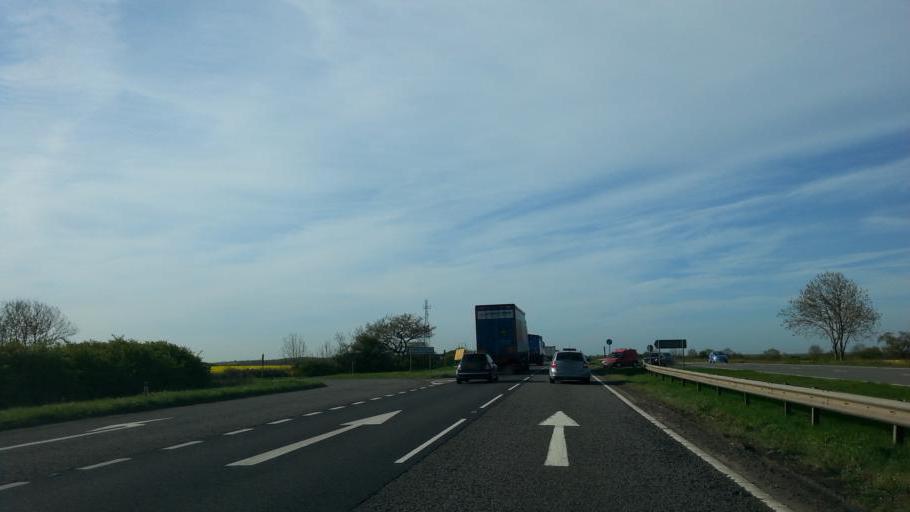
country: GB
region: England
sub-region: District of Rutland
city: Clipsham
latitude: 52.7868
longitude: -0.6107
